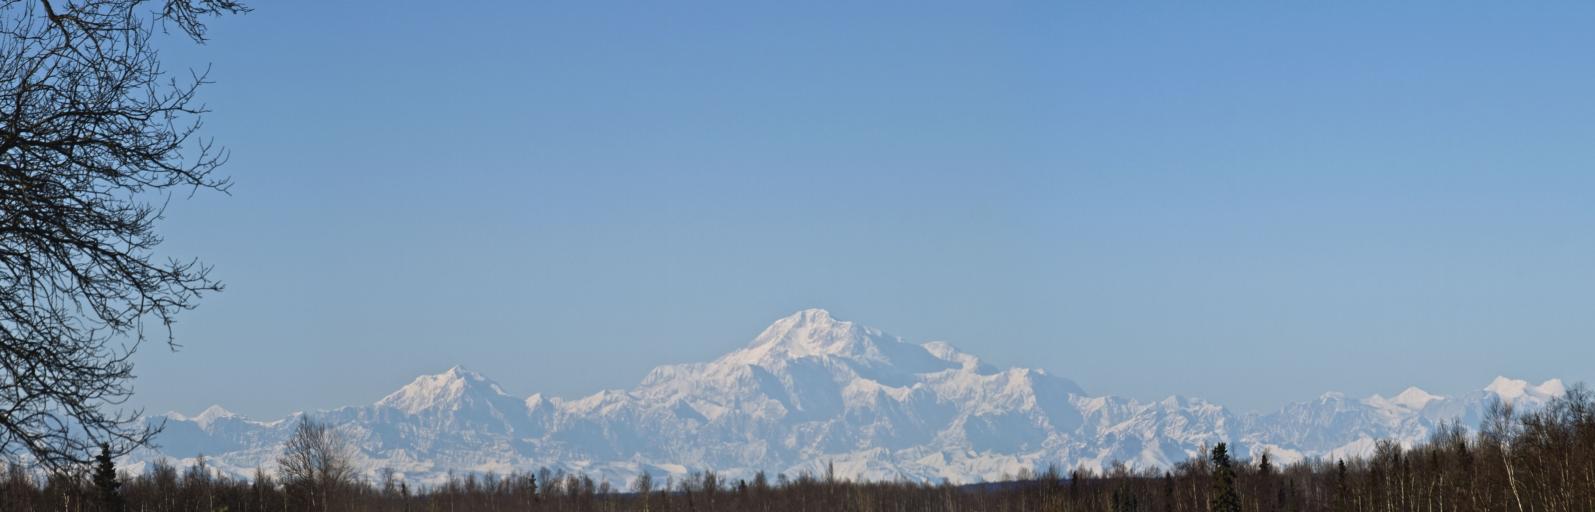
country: US
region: Alaska
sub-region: Matanuska-Susitna Borough
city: Willow
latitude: 61.7352
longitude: -150.0394
